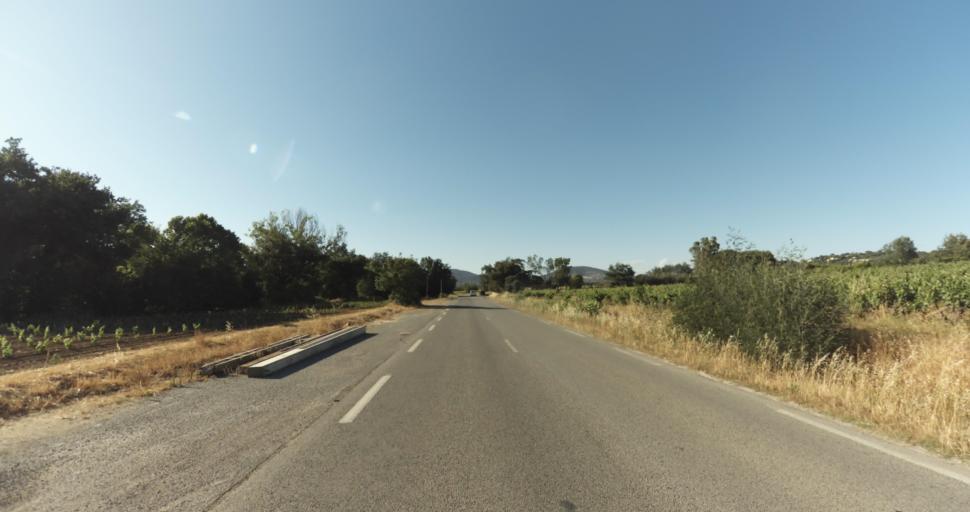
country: FR
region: Provence-Alpes-Cote d'Azur
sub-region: Departement du Var
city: Gassin
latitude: 43.2465
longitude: 6.5944
